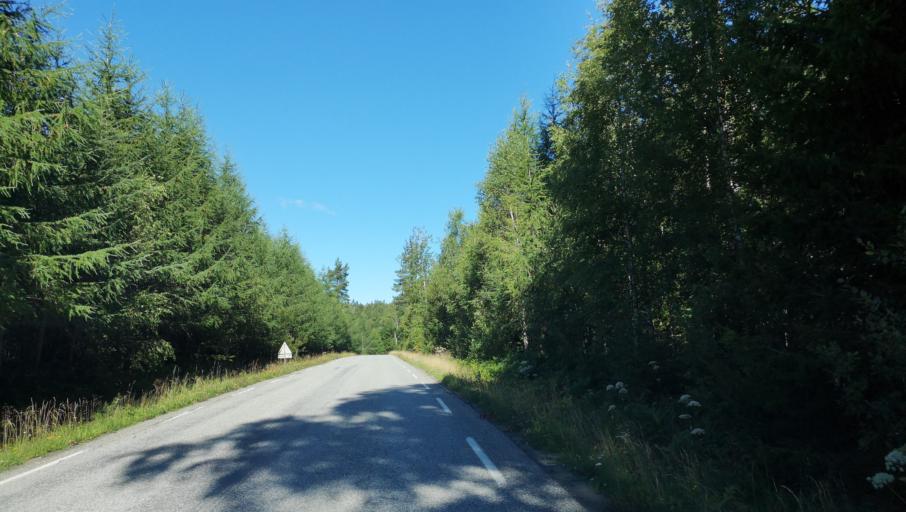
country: NO
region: Ostfold
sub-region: Hobol
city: Knappstad
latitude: 59.6383
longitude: 11.0199
